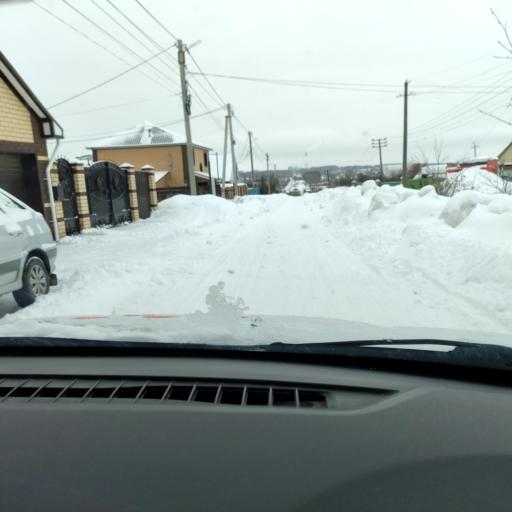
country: RU
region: Bashkortostan
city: Blagoveshchensk
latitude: 55.0508
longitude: 55.9728
